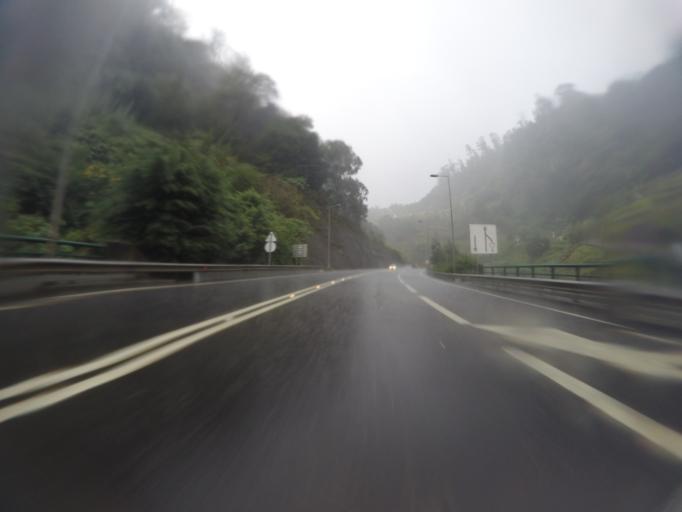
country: PT
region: Madeira
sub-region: Santa Cruz
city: Santa Cruz
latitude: 32.7348
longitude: -16.8063
